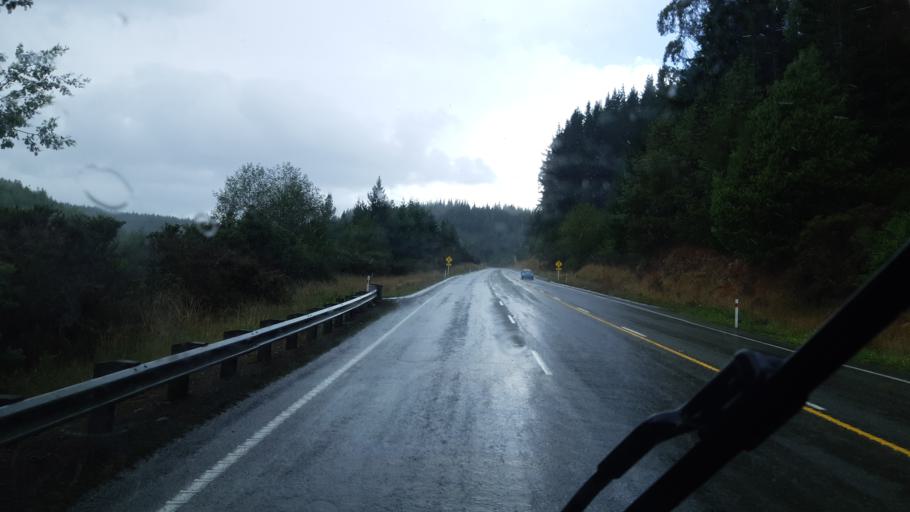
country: NZ
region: Tasman
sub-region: Tasman District
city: Wakefield
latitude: -41.4861
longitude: 172.9012
